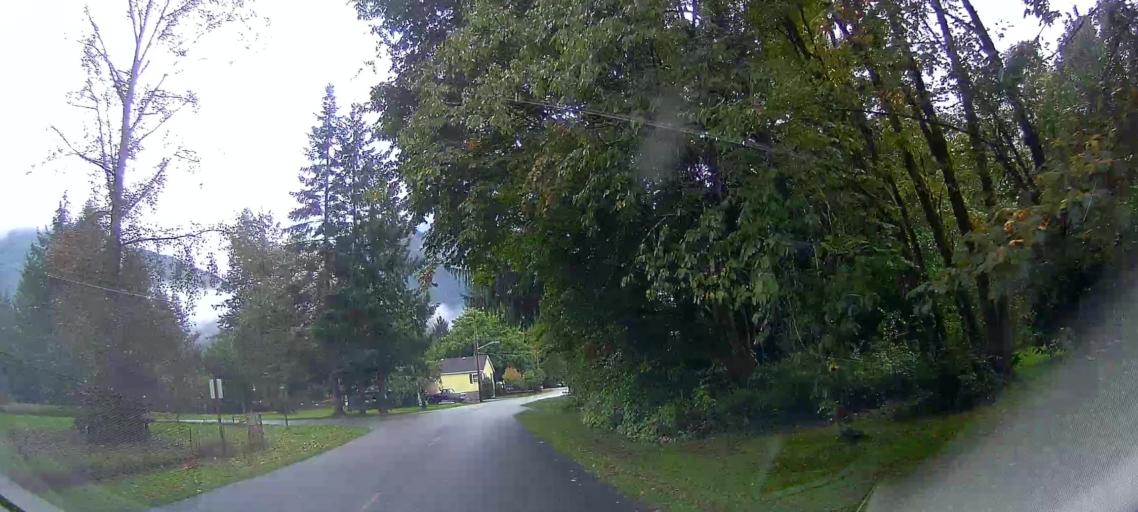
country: US
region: Washington
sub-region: Skagit County
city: Sedro-Woolley
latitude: 48.5241
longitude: -121.9903
